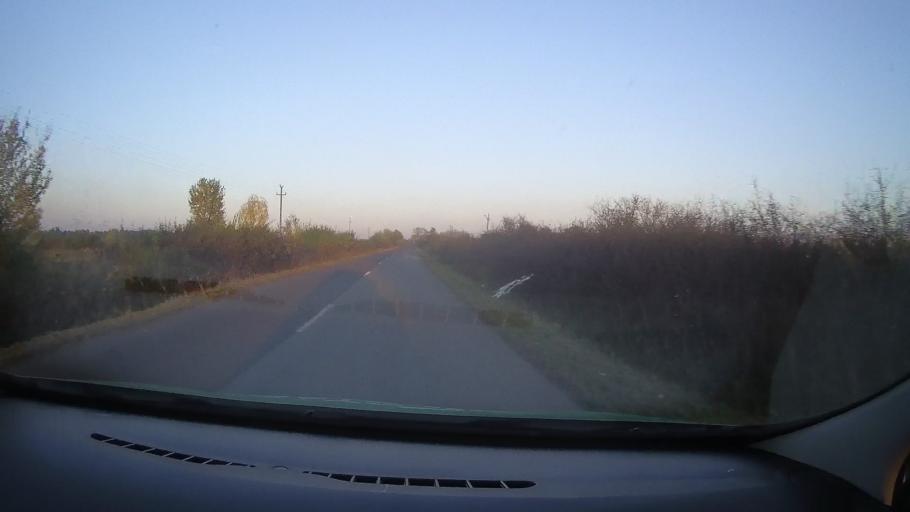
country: RO
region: Timis
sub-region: Comuna Manastiur
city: Manastiur
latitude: 45.8359
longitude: 22.0464
